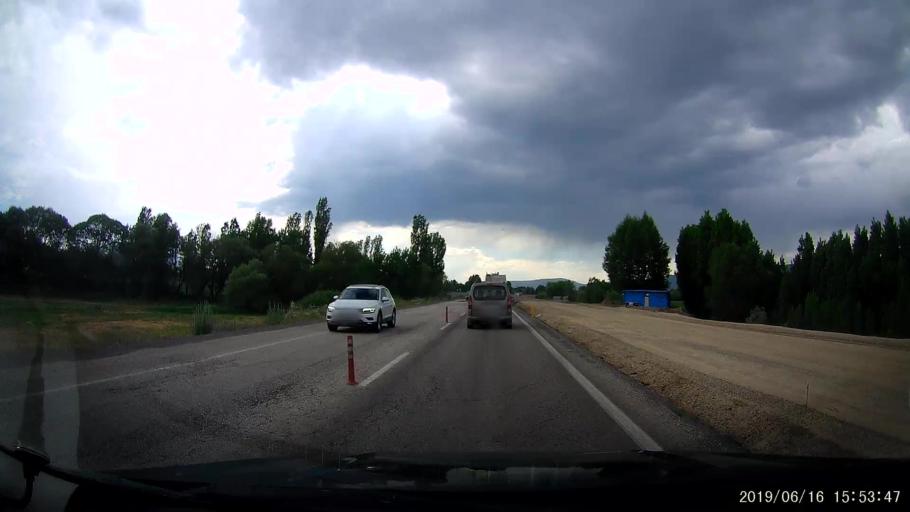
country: TR
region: Erzurum
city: Pasinler
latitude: 39.9775
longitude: 41.6423
